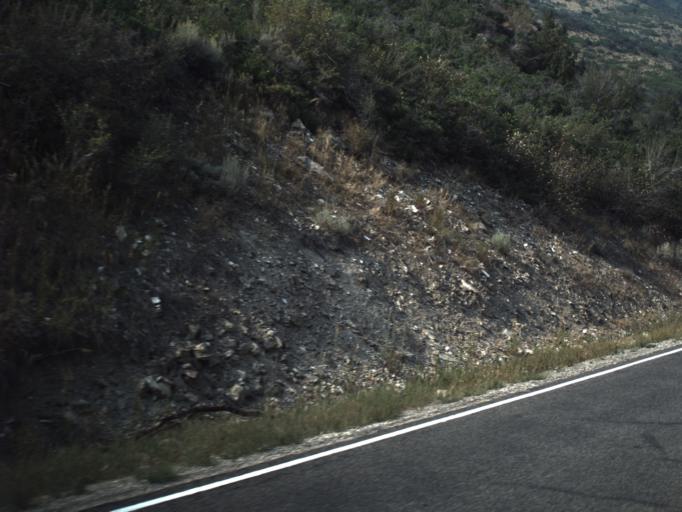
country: US
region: Utah
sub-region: Summit County
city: Francis
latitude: 40.6214
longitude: -111.2055
